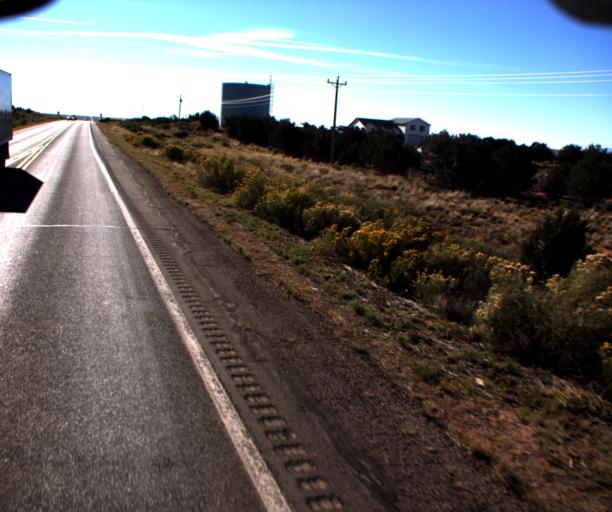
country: US
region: Arizona
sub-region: Mohave County
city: Colorado City
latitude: 36.9610
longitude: -112.9674
